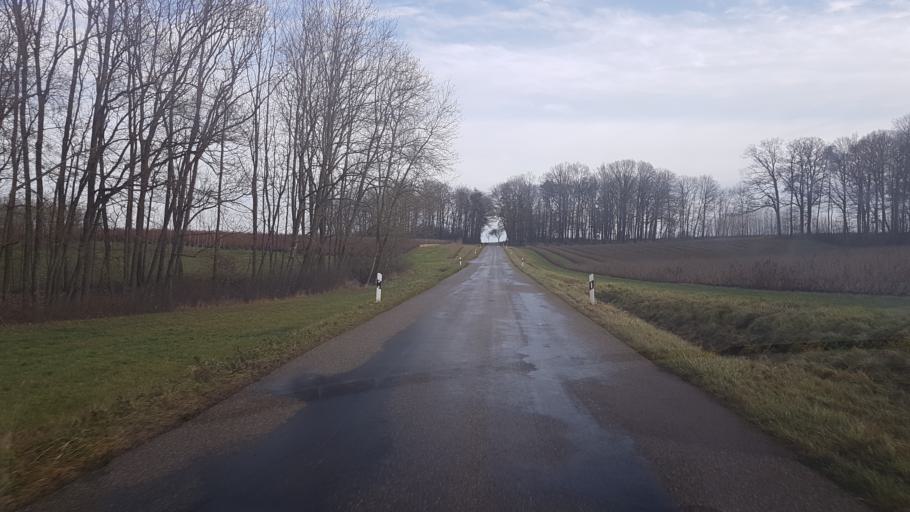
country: DE
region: Baden-Wuerttemberg
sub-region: Regierungsbezirk Stuttgart
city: Wallhausen
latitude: 49.2301
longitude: 10.0771
